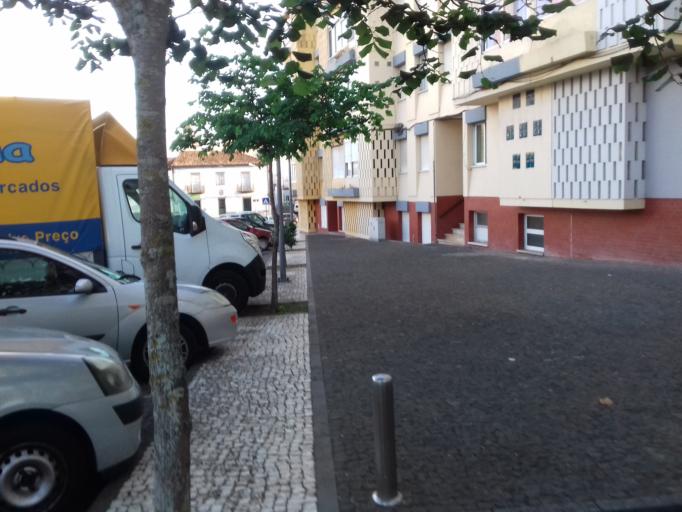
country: PT
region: Azores
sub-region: Ponta Delgada
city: Rosto de Cao
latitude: 37.7432
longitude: -25.6569
